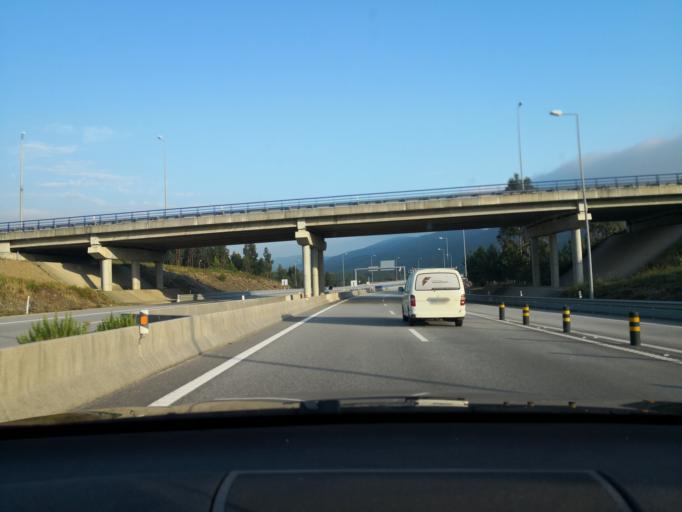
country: PT
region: Porto
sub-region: Paredes
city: Recarei
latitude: 41.1390
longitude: -8.4264
